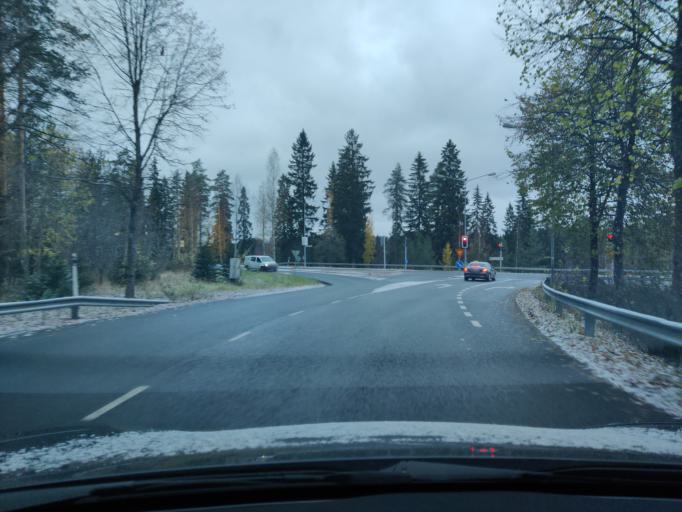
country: FI
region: Northern Savo
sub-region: Kuopio
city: Kuopio
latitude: 62.8418
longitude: 27.6339
